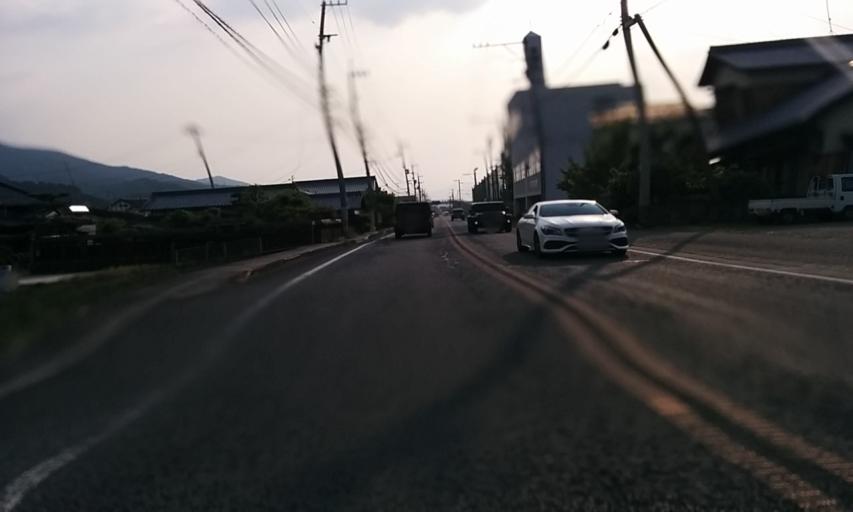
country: JP
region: Ehime
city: Saijo
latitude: 33.8996
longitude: 133.1801
